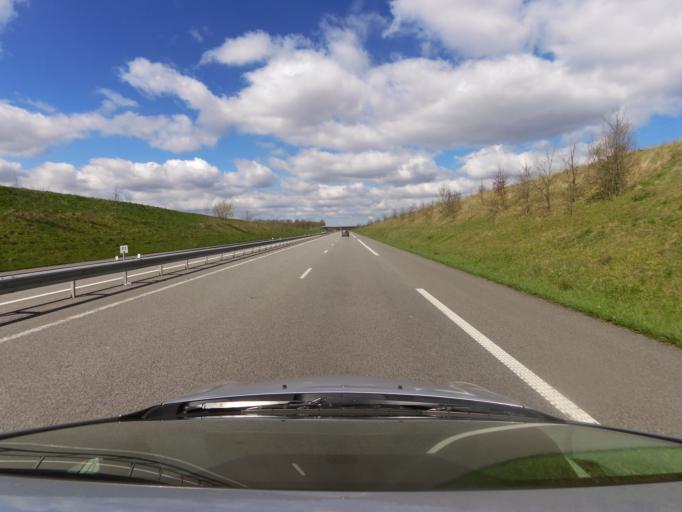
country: FR
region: Haute-Normandie
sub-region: Departement de la Seine-Maritime
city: Limesy
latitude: 49.6531
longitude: 0.9521
